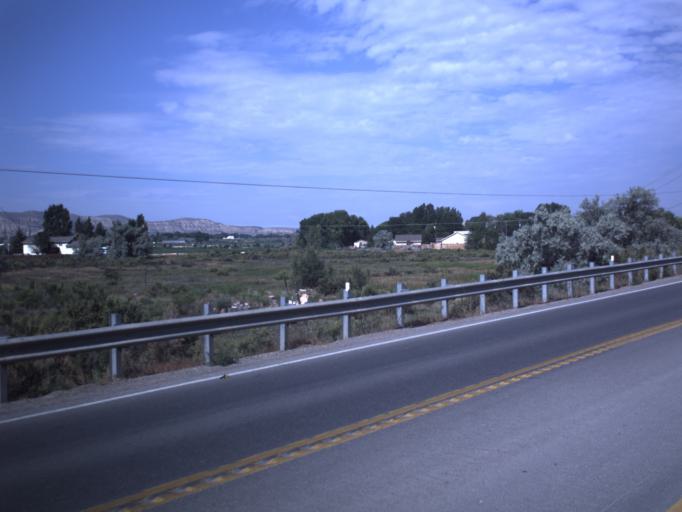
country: US
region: Utah
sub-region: Uintah County
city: Naples
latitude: 40.4047
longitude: -109.4766
